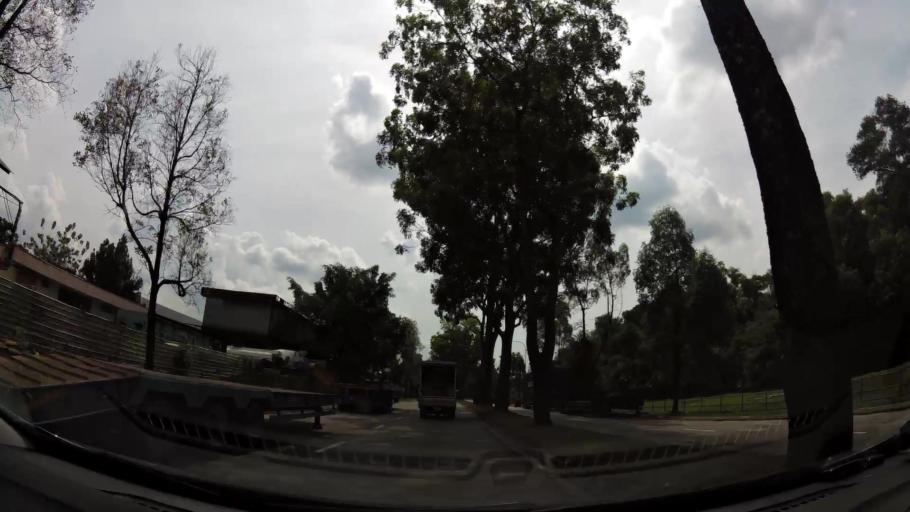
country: MY
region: Johor
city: Johor Bahru
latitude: 1.4233
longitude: 103.7444
